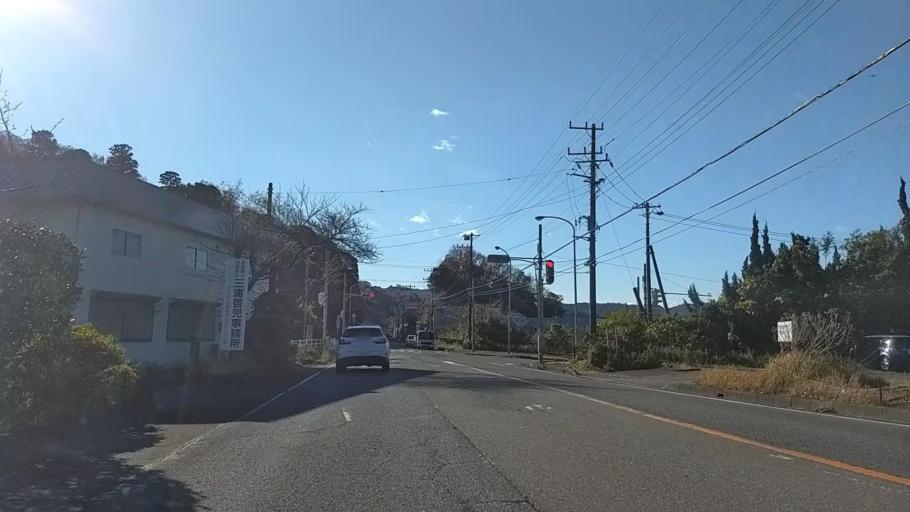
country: JP
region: Chiba
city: Futtsu
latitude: 35.2270
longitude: 139.8739
